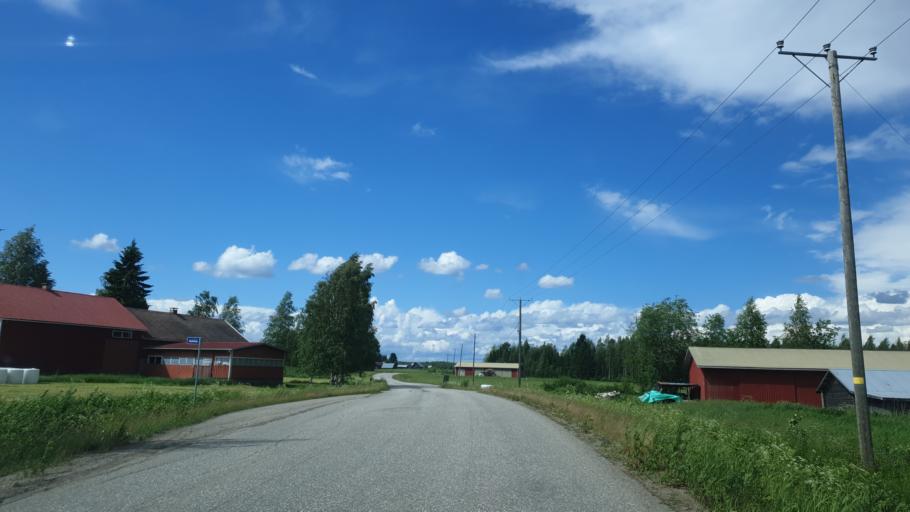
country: FI
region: Northern Savo
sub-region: Koillis-Savo
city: Kaavi
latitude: 62.9897
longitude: 28.7284
